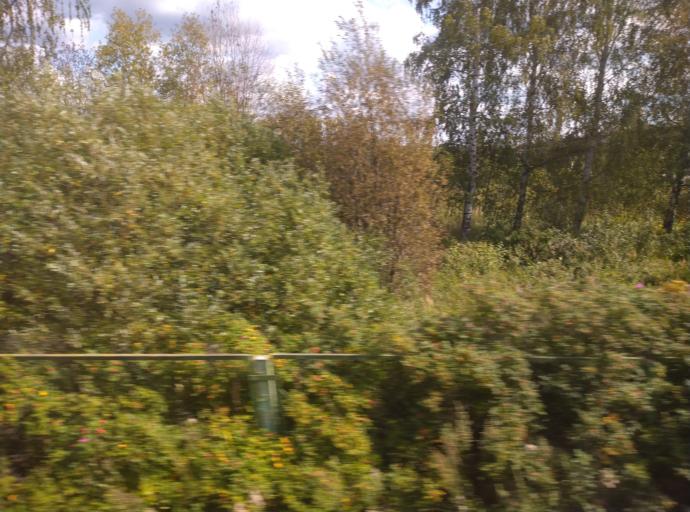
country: RU
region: St.-Petersburg
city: Kolpino
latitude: 59.7340
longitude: 30.6339
